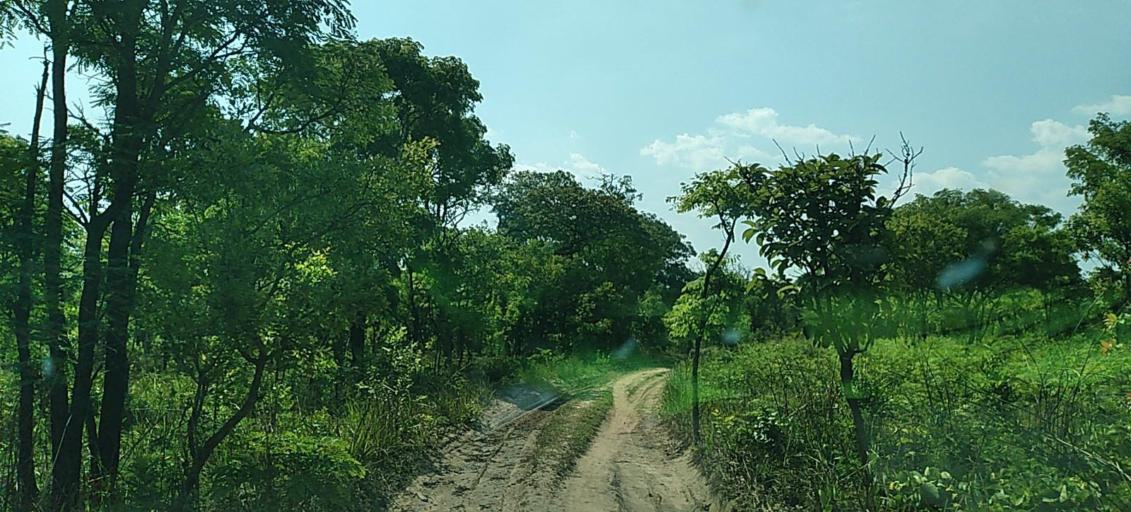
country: ZM
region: North-Western
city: Mwinilunga
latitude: -11.2720
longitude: 24.9794
